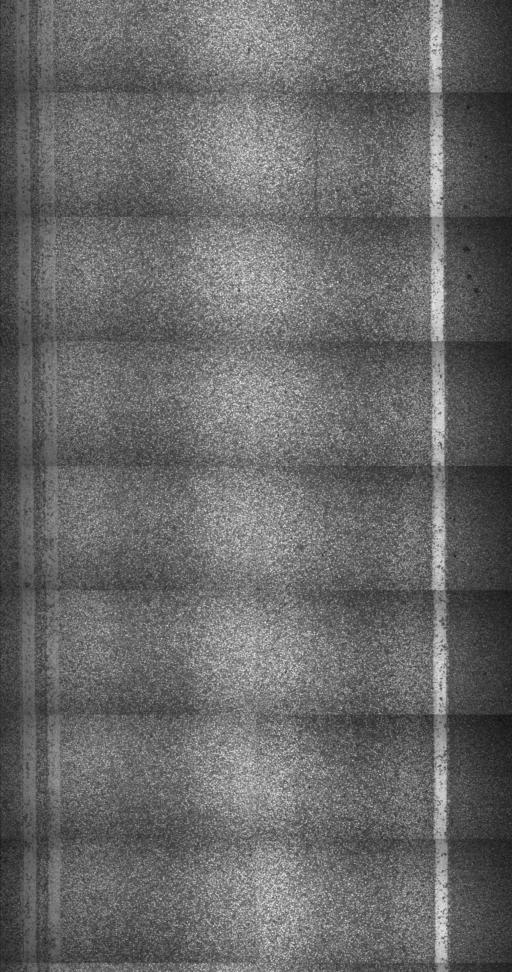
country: US
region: Vermont
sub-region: Lamoille County
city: Morristown
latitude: 44.5129
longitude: -72.7663
